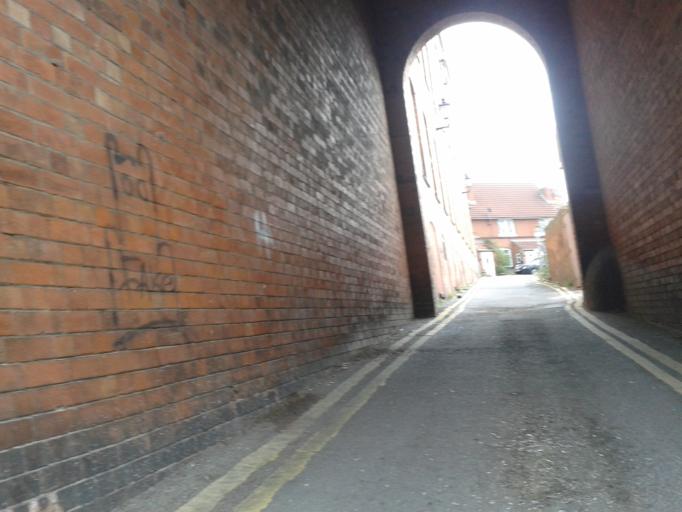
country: GB
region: England
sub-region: Leicestershire
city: Hinckley
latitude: 52.5429
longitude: -1.3735
